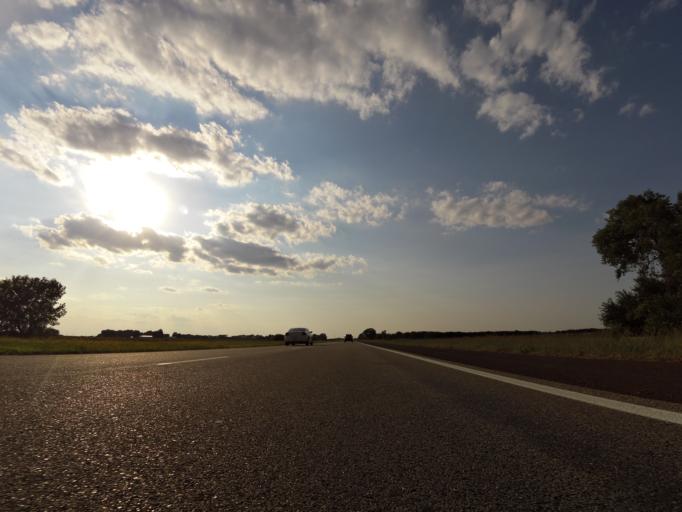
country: US
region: Kansas
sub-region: Reno County
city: Haven
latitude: 37.9160
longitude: -97.8208
